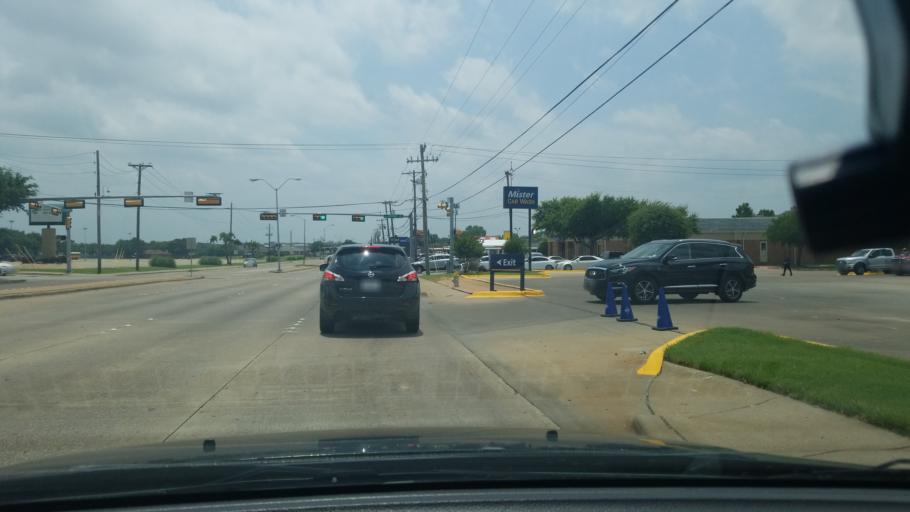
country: US
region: Texas
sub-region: Dallas County
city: Mesquite
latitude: 32.8089
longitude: -96.6113
